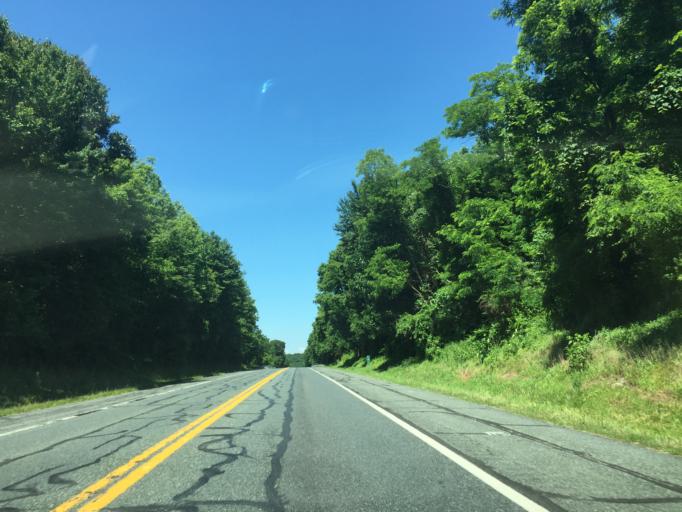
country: US
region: Maryland
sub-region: Harford County
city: Bel Air North
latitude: 39.5748
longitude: -76.4263
